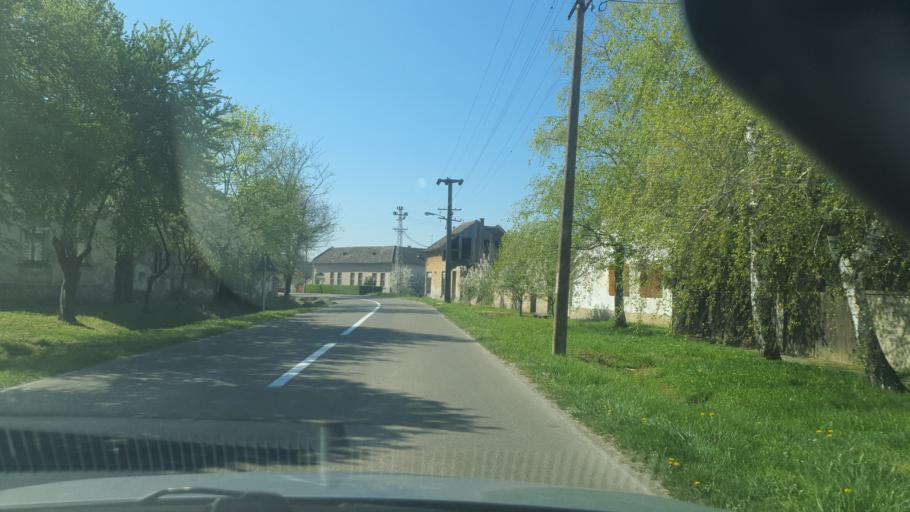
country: RS
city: Kolut
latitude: 45.8903
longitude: 18.9240
